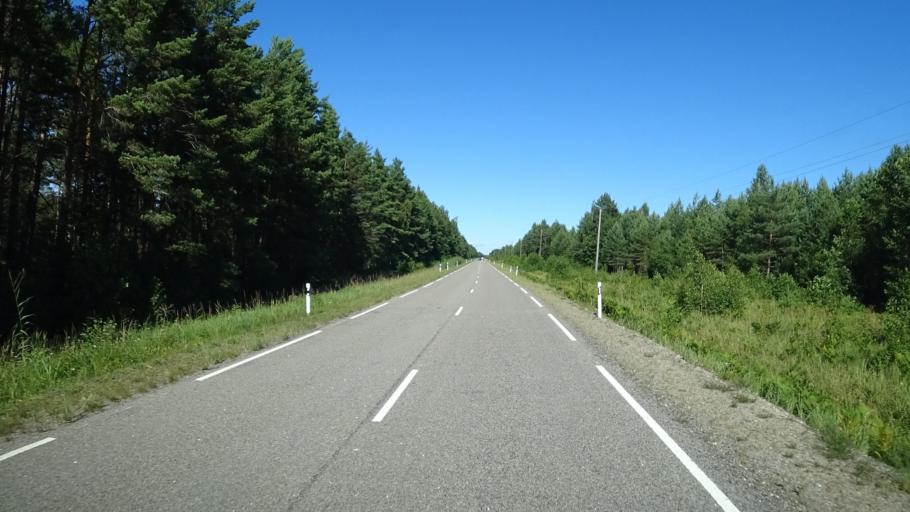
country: LV
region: Dundaga
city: Dundaga
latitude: 57.6998
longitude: 22.4174
